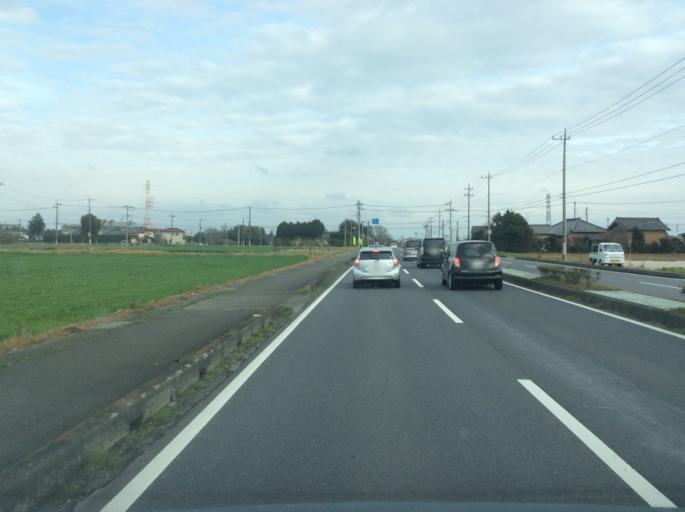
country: JP
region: Ibaraki
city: Naka
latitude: 36.1293
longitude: 140.1645
